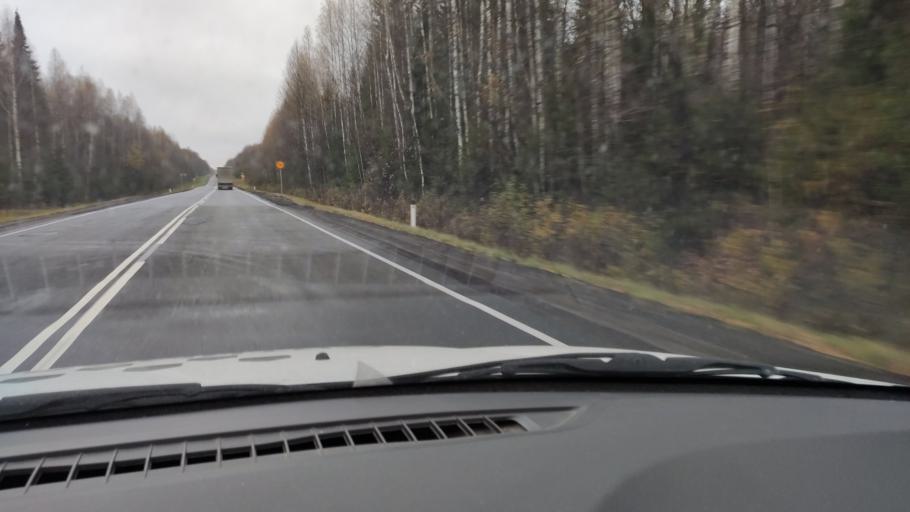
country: RU
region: Kirov
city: Omutninsk
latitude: 58.7643
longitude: 51.9908
